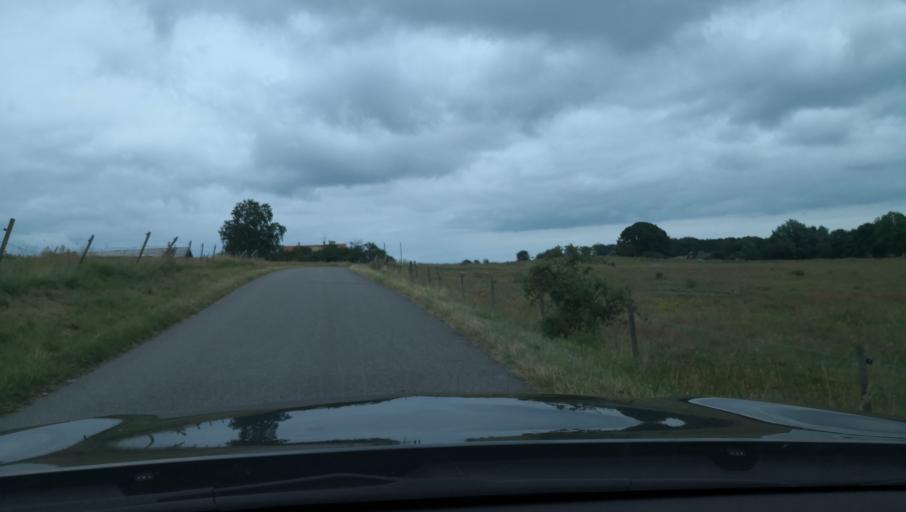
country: SE
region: Skane
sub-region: Simrishamns Kommun
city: Kivik
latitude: 55.7234
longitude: 14.1791
